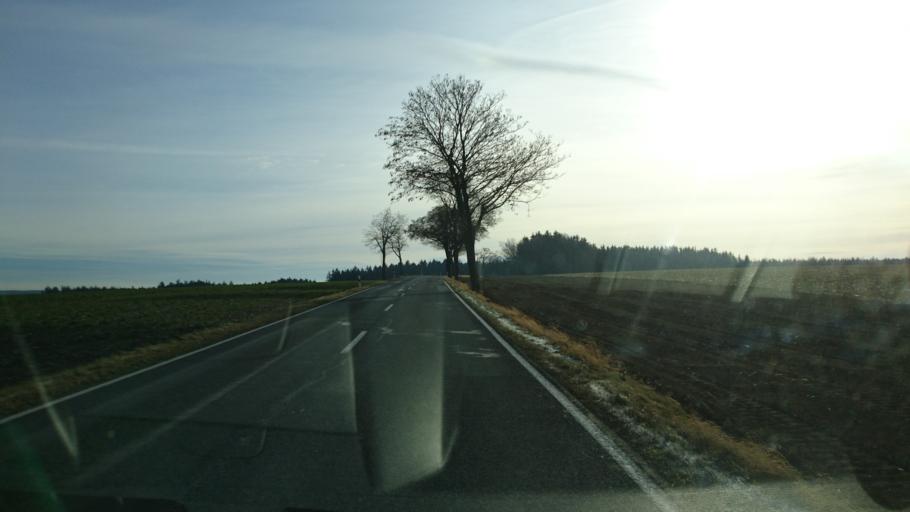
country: DE
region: Thuringia
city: Tanna
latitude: 50.5263
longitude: 11.8782
